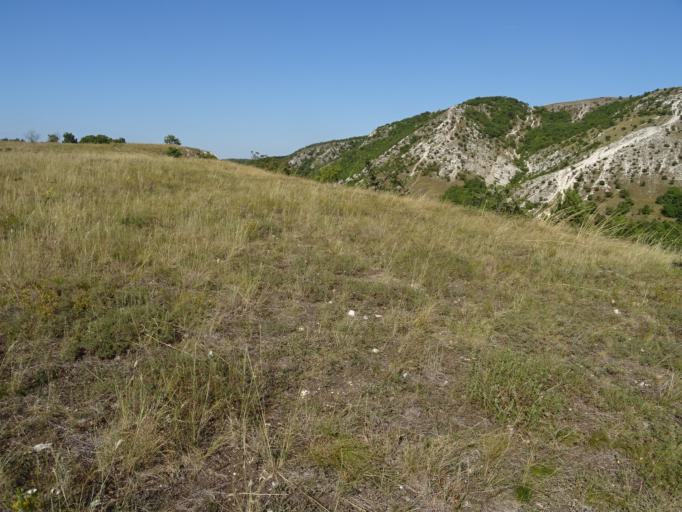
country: HU
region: Veszprem
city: Varpalota
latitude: 47.2175
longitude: 18.1932
